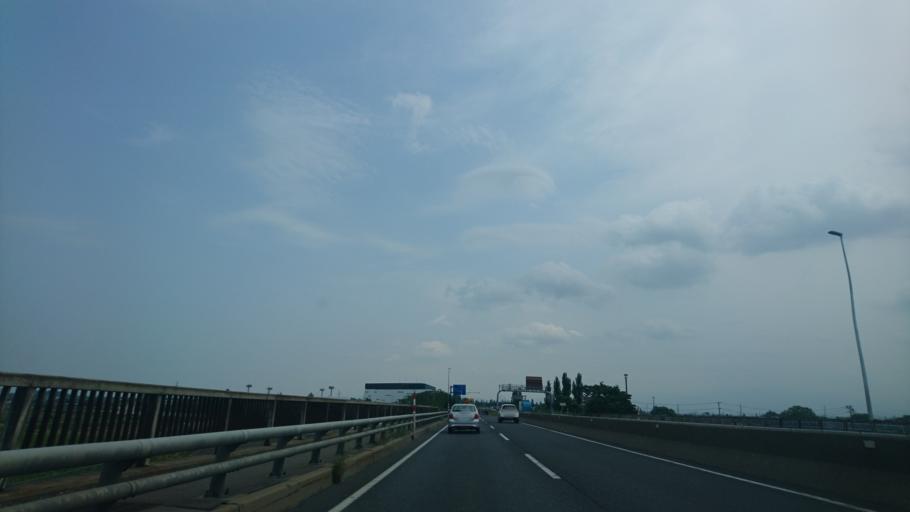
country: JP
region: Niigata
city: Kameda-honcho
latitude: 37.9345
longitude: 139.1490
